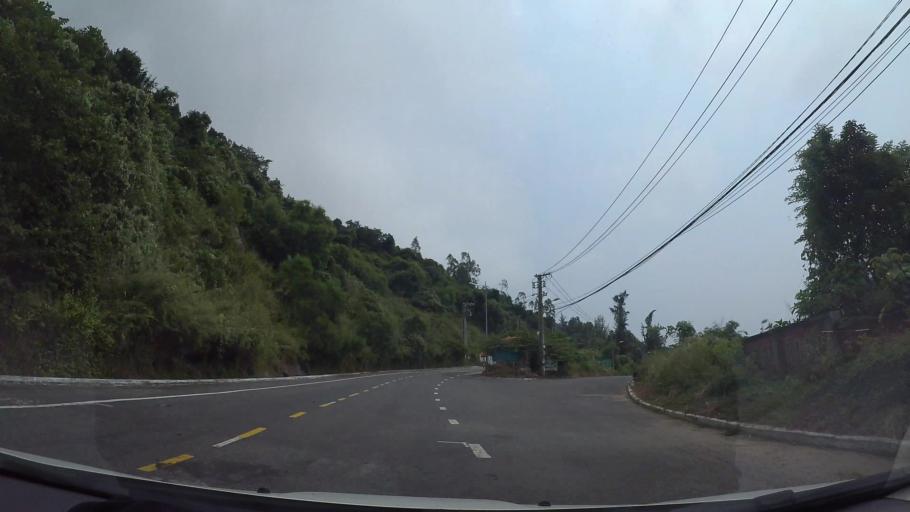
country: VN
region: Da Nang
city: Son Tra
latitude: 16.1055
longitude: 108.3002
